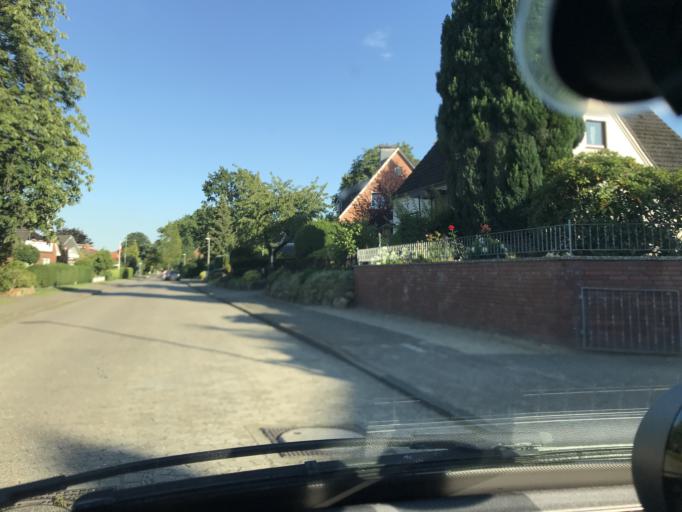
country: DE
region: Lower Saxony
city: Buxtehude
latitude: 53.4582
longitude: 9.7248
